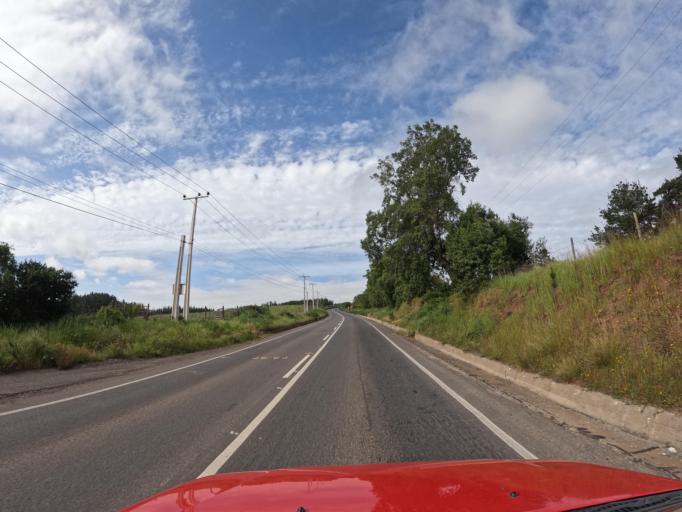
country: CL
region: O'Higgins
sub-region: Provincia de Colchagua
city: Santa Cruz
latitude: -34.3640
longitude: -71.9515
